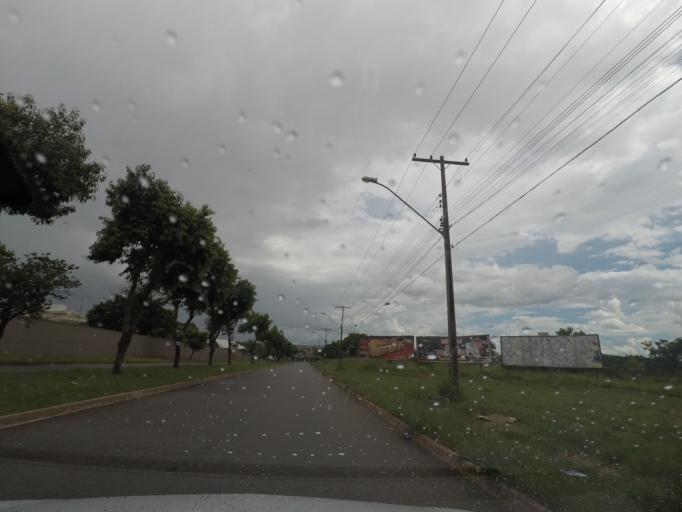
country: BR
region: Goias
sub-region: Goiania
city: Goiania
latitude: -16.7158
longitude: -49.3332
